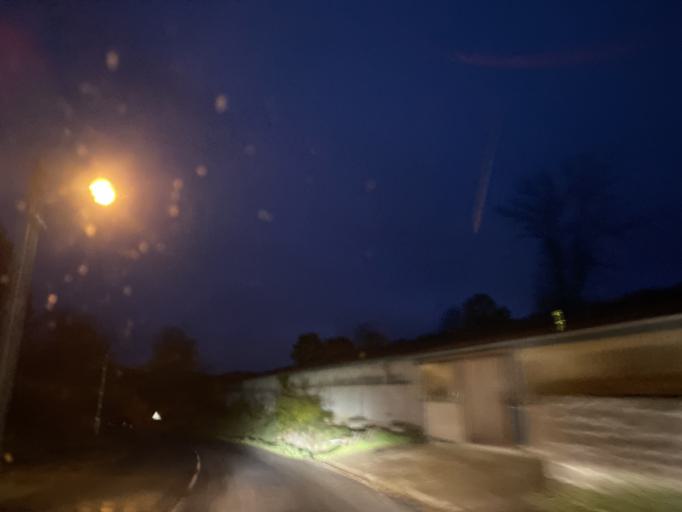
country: FR
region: Auvergne
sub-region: Departement du Puy-de-Dome
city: Cunlhat
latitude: 45.6062
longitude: 3.5193
